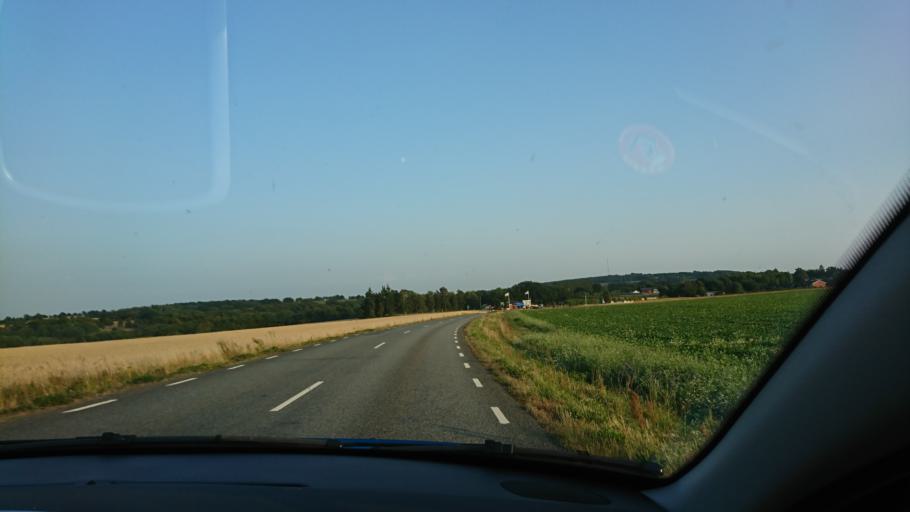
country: SE
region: Skane
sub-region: Simrishamns Kommun
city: Kivik
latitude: 55.6934
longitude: 14.1571
